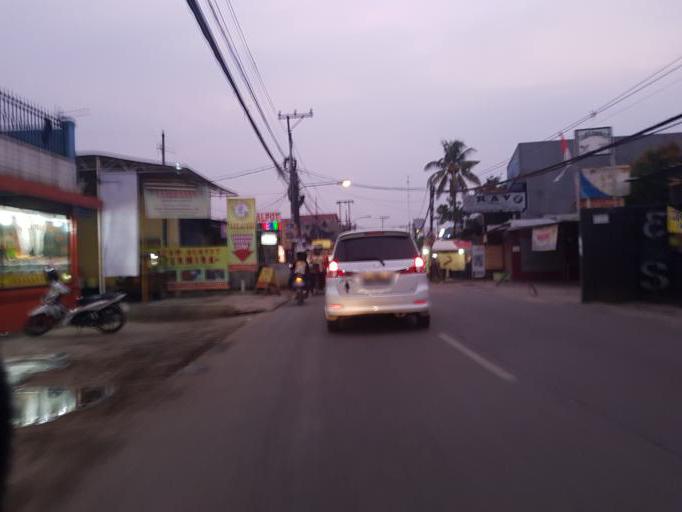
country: ID
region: West Java
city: Bekasi
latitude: -6.2943
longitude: 106.9199
